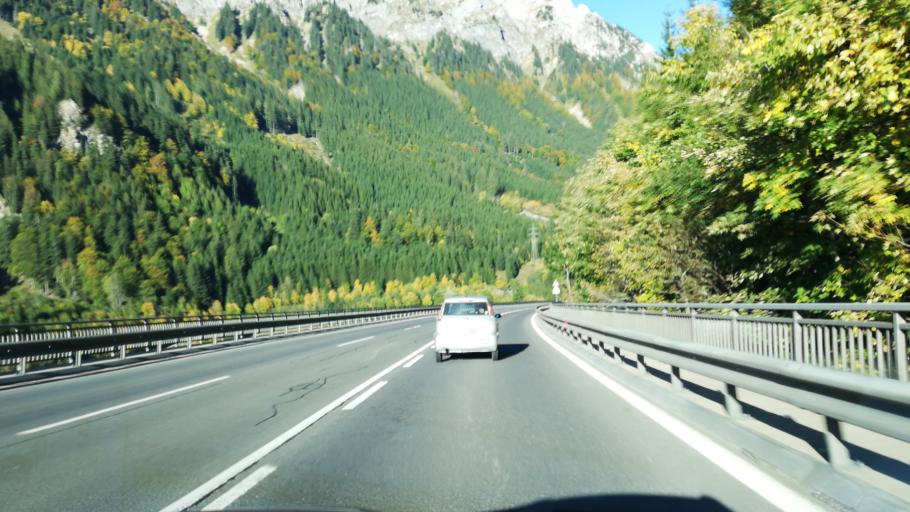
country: AT
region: Styria
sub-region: Politischer Bezirk Leoben
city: Eisenerz
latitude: 47.5467
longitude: 14.9321
